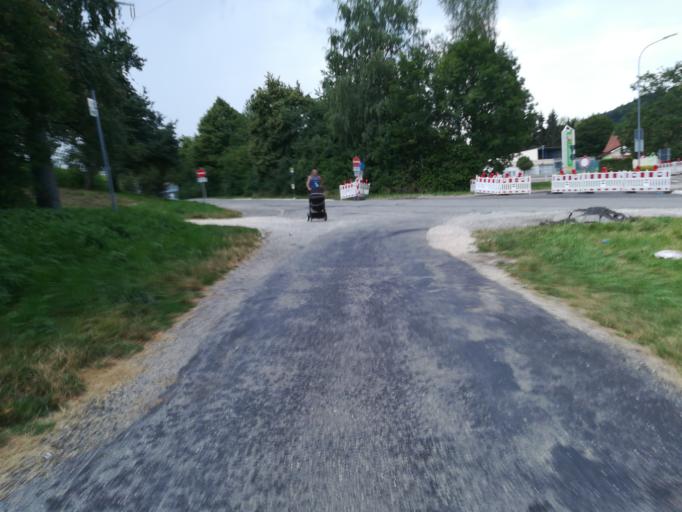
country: DE
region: Baden-Wuerttemberg
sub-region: Freiburg Region
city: Hilzingen
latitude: 47.7609
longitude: 8.8031
